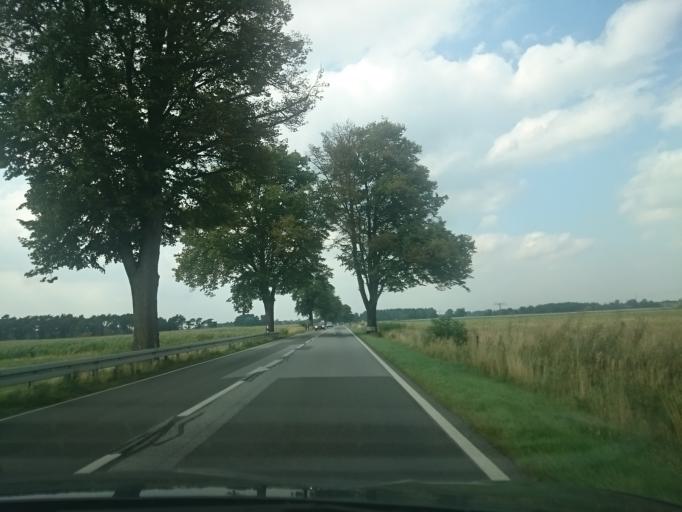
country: DE
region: Mecklenburg-Vorpommern
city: Ferdinandshof
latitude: 53.6962
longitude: 13.8731
